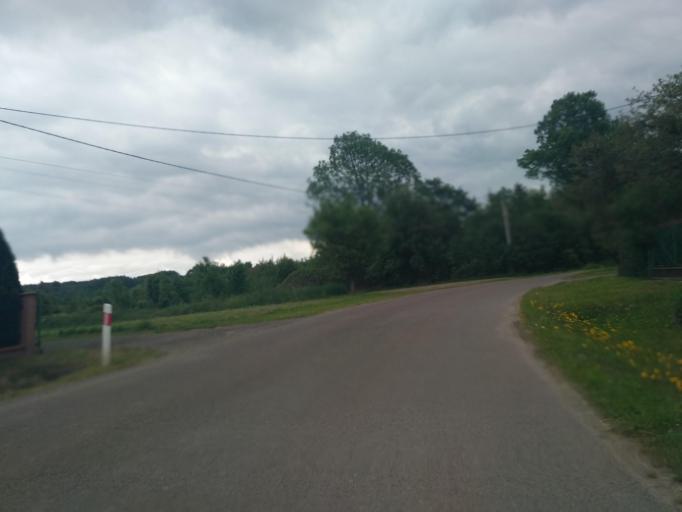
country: PL
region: Subcarpathian Voivodeship
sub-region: Powiat jasielski
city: Tarnowiec
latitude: 49.6753
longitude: 21.5792
